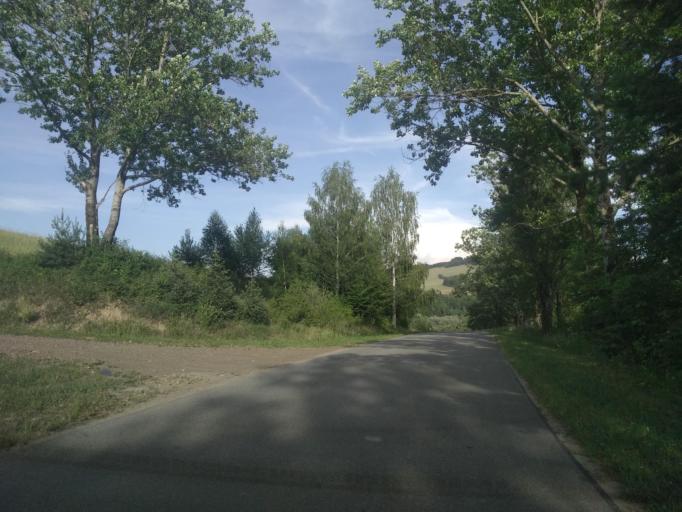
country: PL
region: Subcarpathian Voivodeship
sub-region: Powiat sanocki
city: Rzepedz
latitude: 49.4294
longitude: 22.1318
